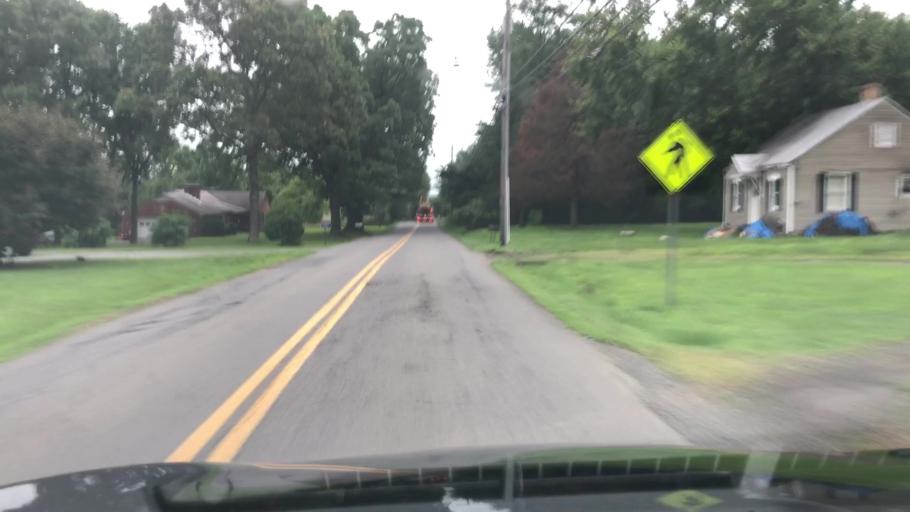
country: US
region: Virginia
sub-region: Prince William County
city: Nokesville
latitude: 38.6587
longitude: -77.6432
